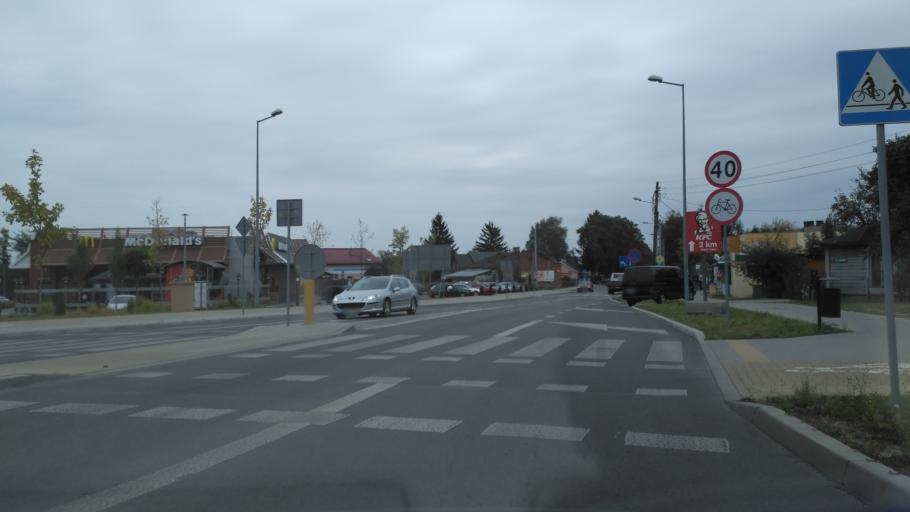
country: PL
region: Lublin Voivodeship
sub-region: Chelm
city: Chelm
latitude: 51.1460
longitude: 23.4373
